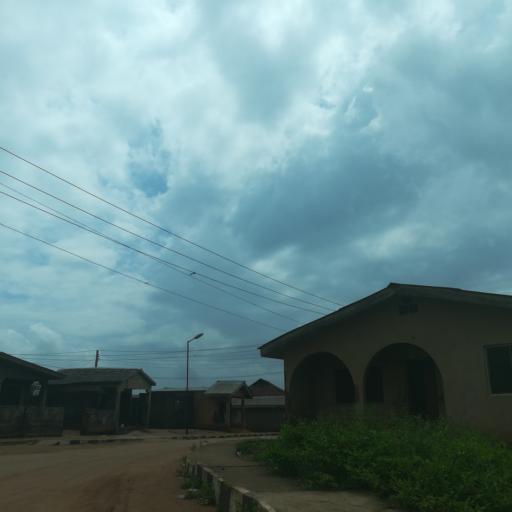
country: NG
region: Lagos
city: Ejirin
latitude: 6.6425
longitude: 3.7108
